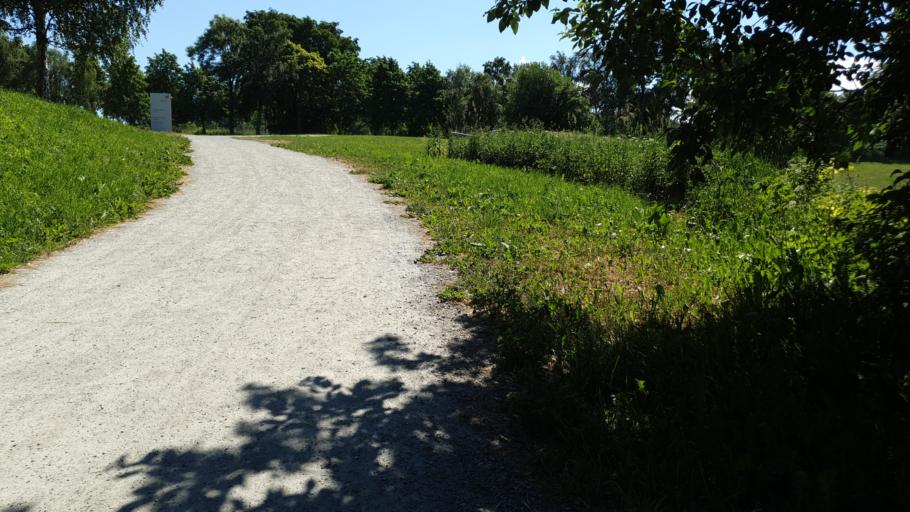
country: NO
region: Sor-Trondelag
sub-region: Trondheim
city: Trondheim
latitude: 63.4387
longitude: 10.4762
